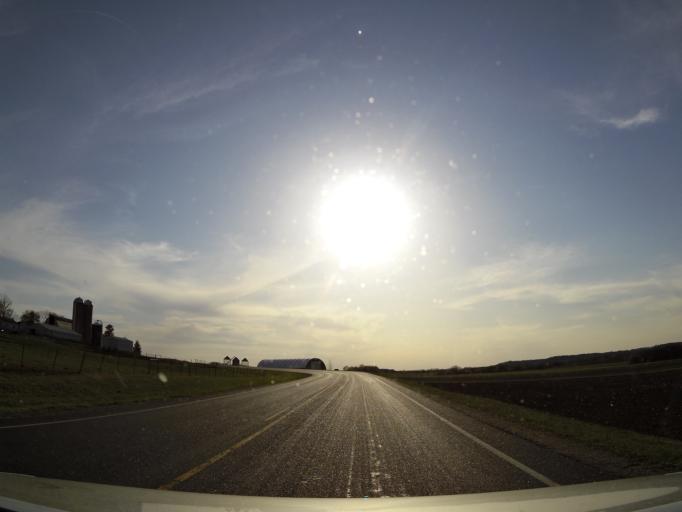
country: US
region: Wisconsin
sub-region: Pierce County
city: River Falls
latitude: 44.8335
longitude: -92.6565
